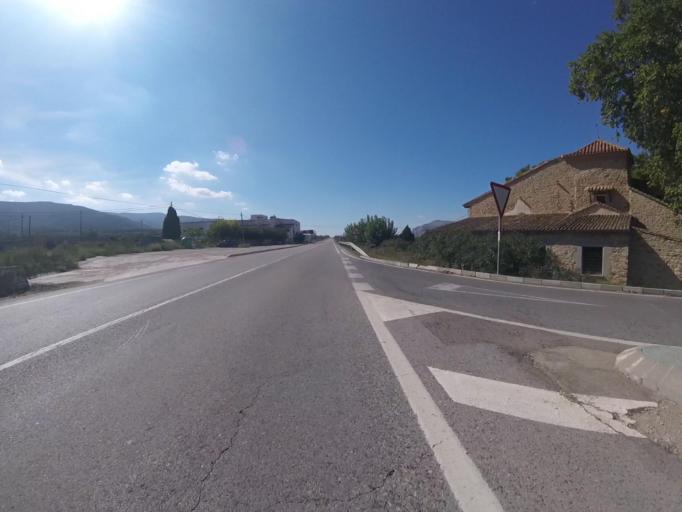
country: ES
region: Valencia
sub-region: Provincia de Castello
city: Albocasser
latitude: 40.3439
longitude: -0.0055
